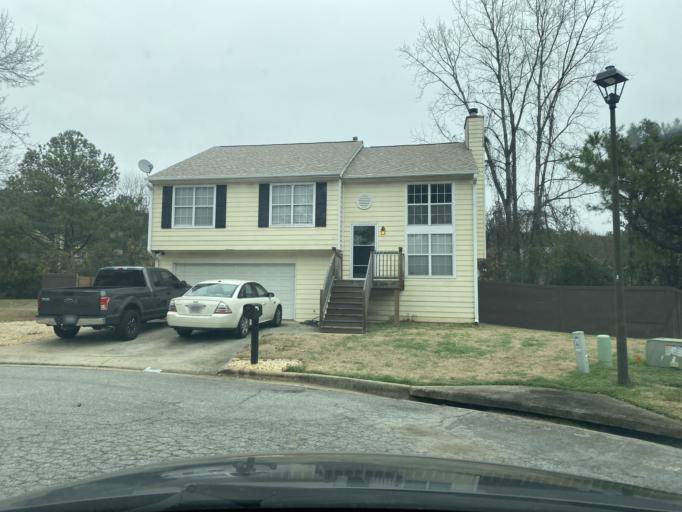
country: US
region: Georgia
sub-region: DeKalb County
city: Pine Mountain
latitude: 33.6877
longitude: -84.1605
